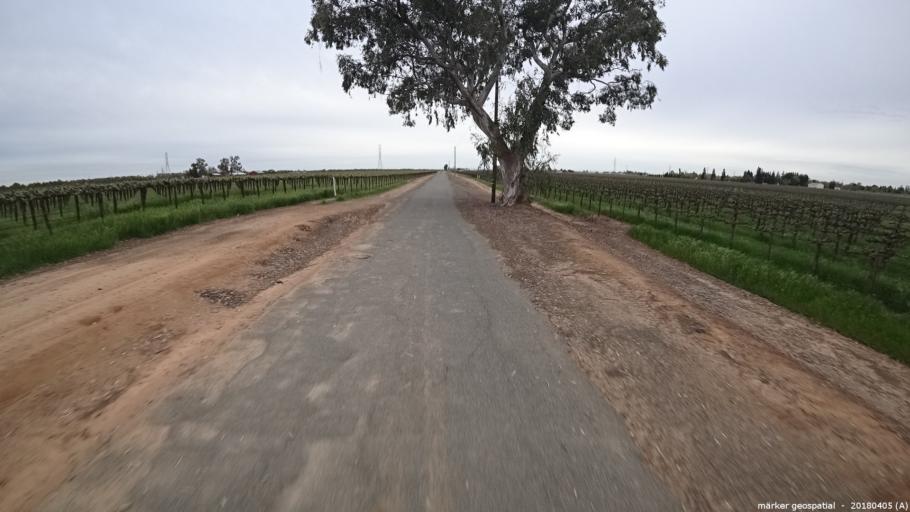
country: US
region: California
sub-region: Sacramento County
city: Herald
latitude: 38.3176
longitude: -121.2285
